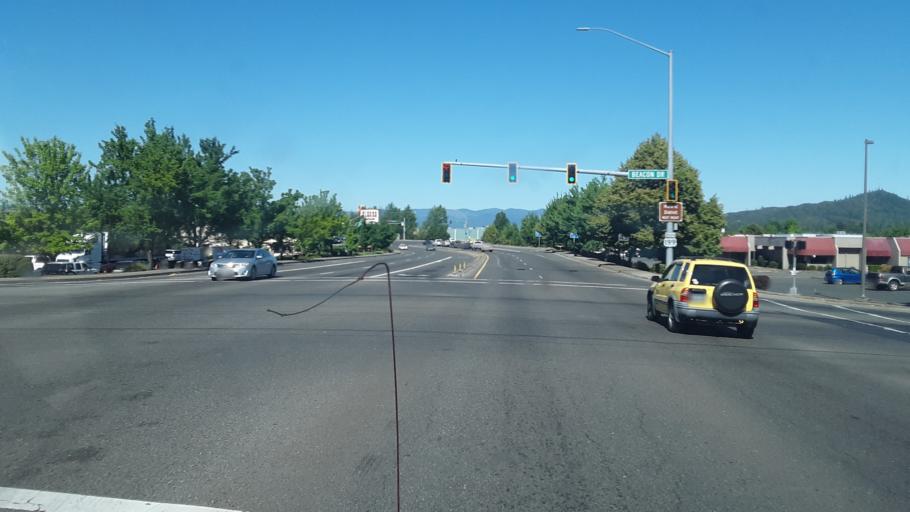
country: US
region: Oregon
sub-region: Josephine County
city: Fruitdale
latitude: 42.4370
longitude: -123.3074
